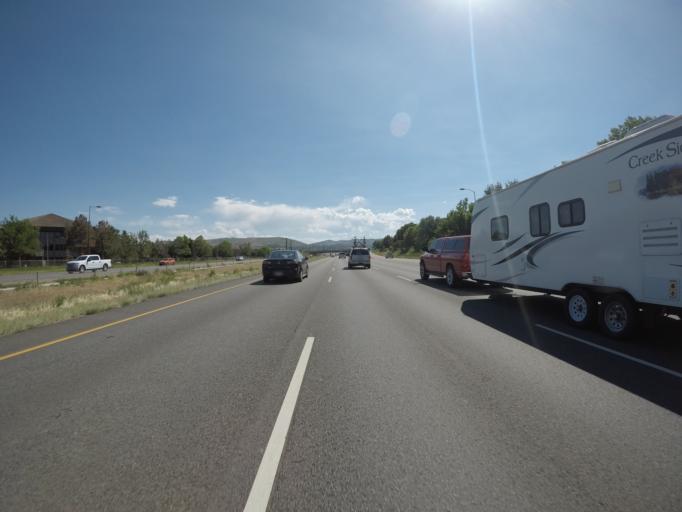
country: US
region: Colorado
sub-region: Jefferson County
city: Applewood
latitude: 39.7433
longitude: -105.1551
